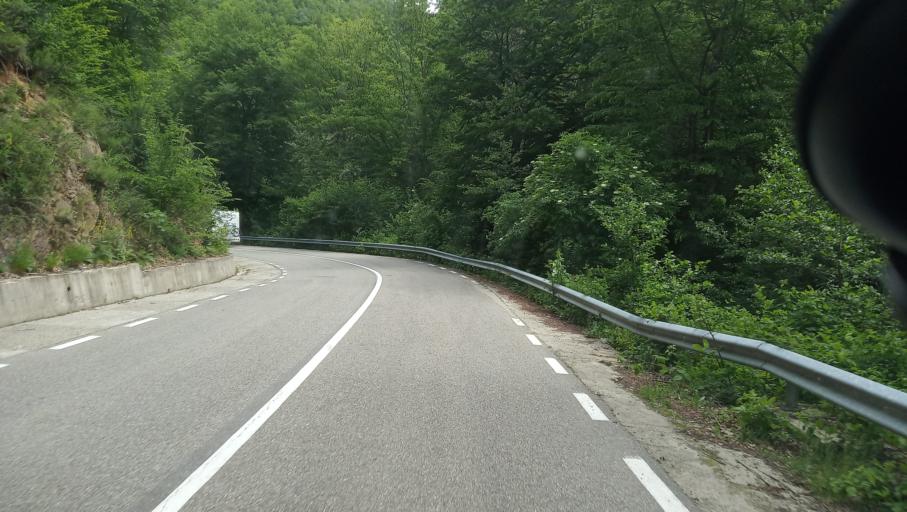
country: RO
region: Caras-Severin
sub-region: Comuna Bucosnita
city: Bucosnita
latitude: 45.2612
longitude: 22.2277
